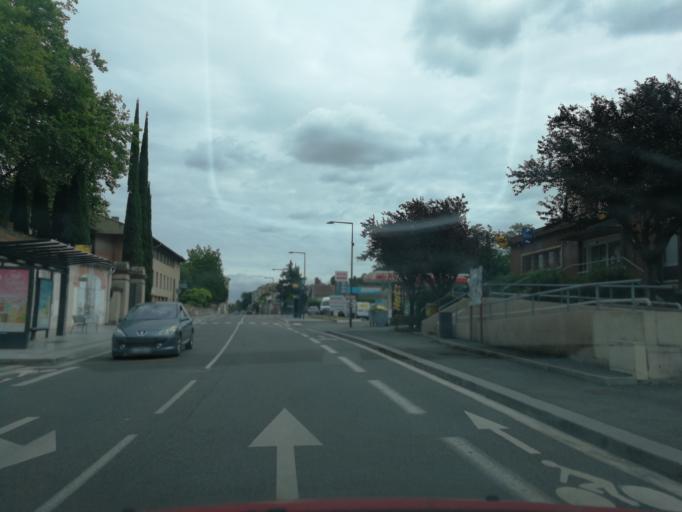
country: FR
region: Midi-Pyrenees
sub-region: Departement de la Haute-Garonne
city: Ramonville-Saint-Agne
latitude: 43.5483
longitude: 1.4720
